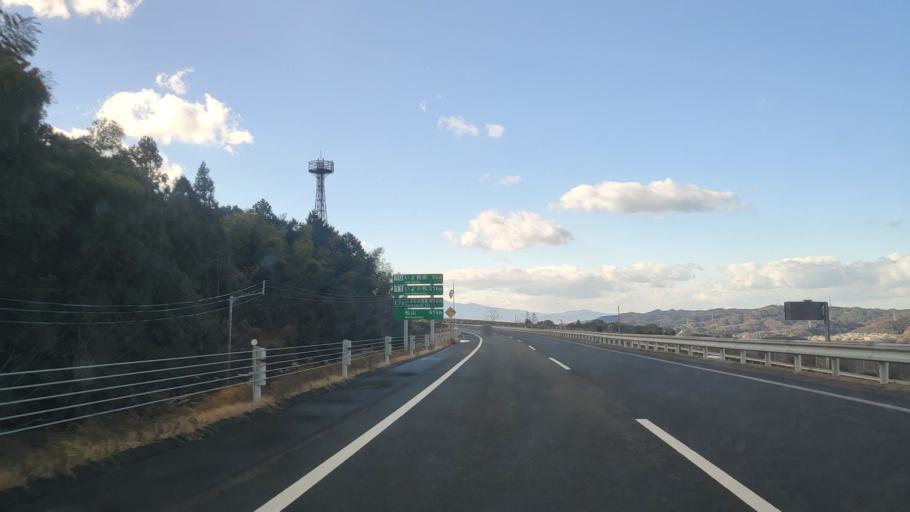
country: JP
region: Ehime
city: Niihama
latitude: 33.9172
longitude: 133.2945
